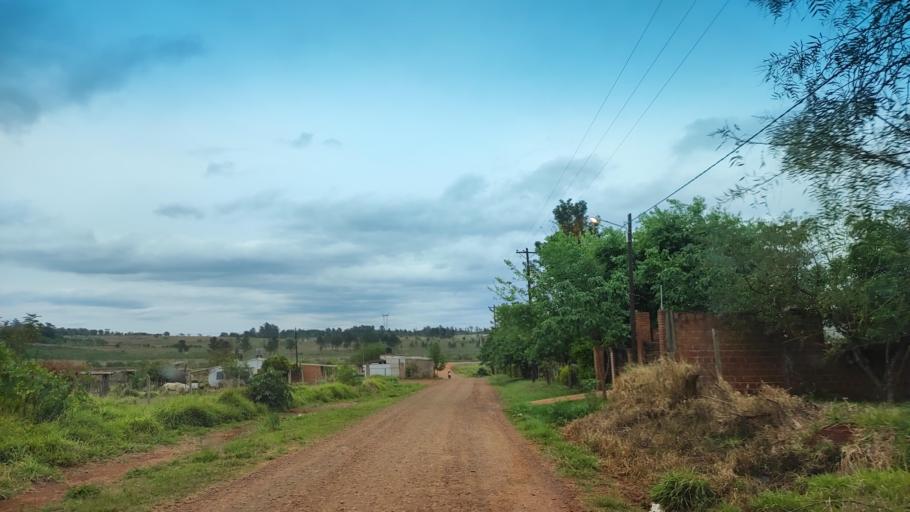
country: AR
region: Misiones
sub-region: Departamento de Capital
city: Posadas
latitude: -27.4671
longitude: -55.9625
